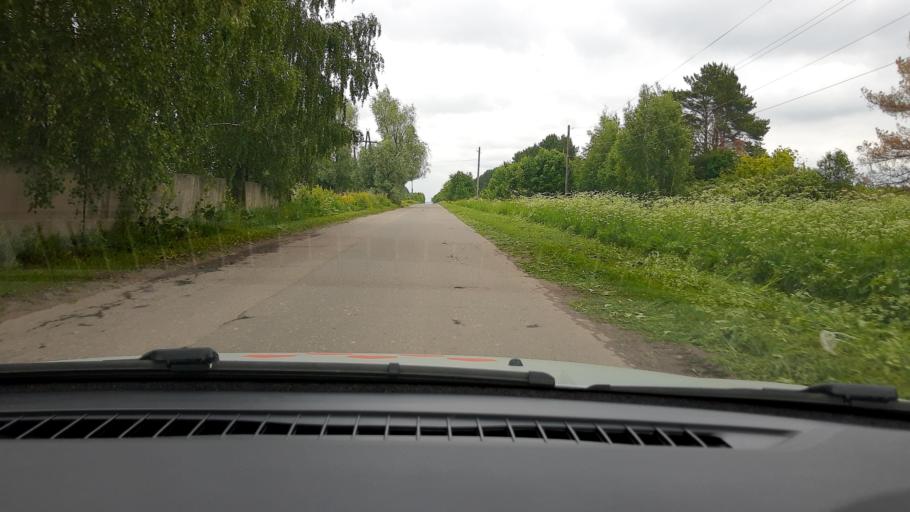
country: RU
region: Nizjnij Novgorod
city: Bogorodsk
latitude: 56.0767
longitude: 43.5106
